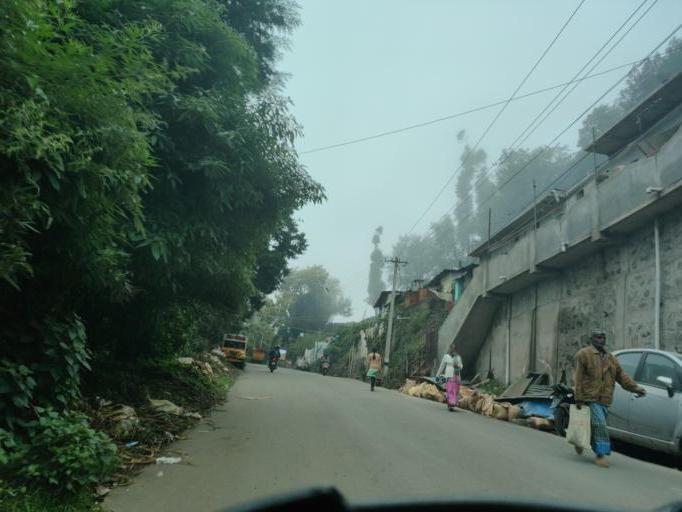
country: IN
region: Tamil Nadu
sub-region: Dindigul
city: Kodaikanal
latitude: 10.2324
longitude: 77.4739
